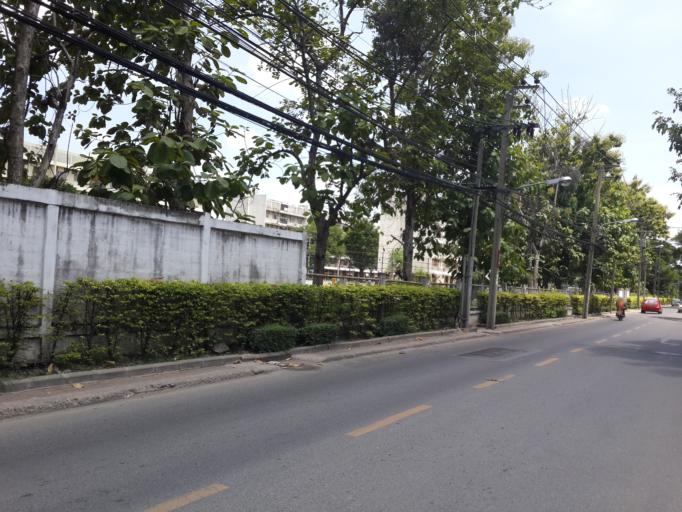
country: TH
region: Bangkok
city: Yan Nawa
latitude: 13.7109
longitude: 100.5423
